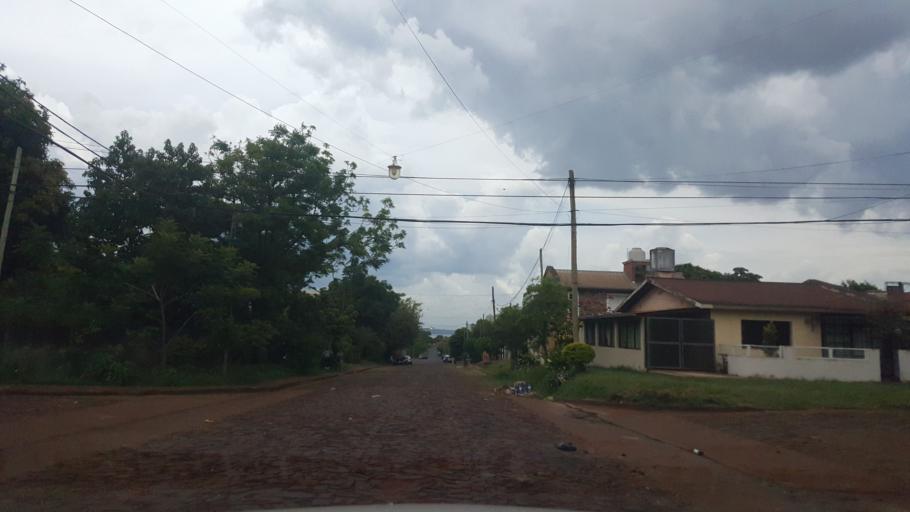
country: AR
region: Misiones
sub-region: Departamento de Capital
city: Posadas
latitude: -27.3889
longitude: -55.9101
